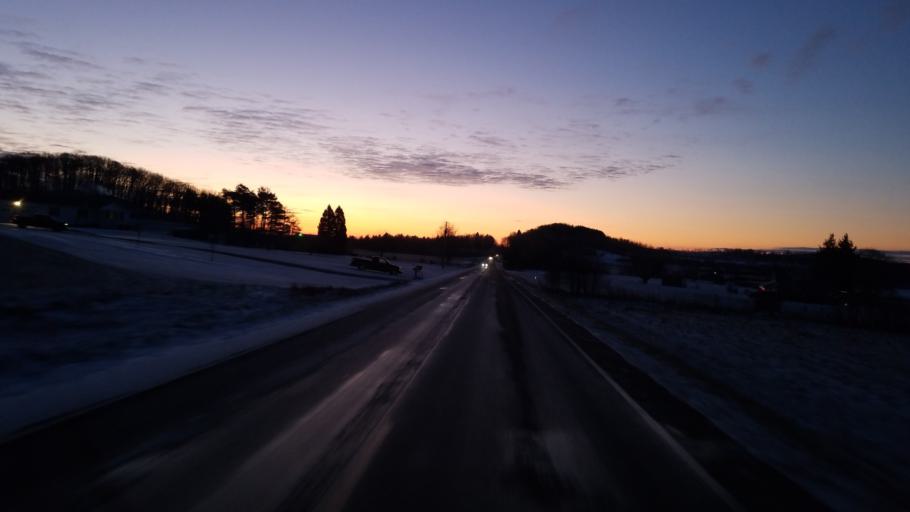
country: US
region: Pennsylvania
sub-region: Clarion County
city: Knox
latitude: 41.2604
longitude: -79.5568
